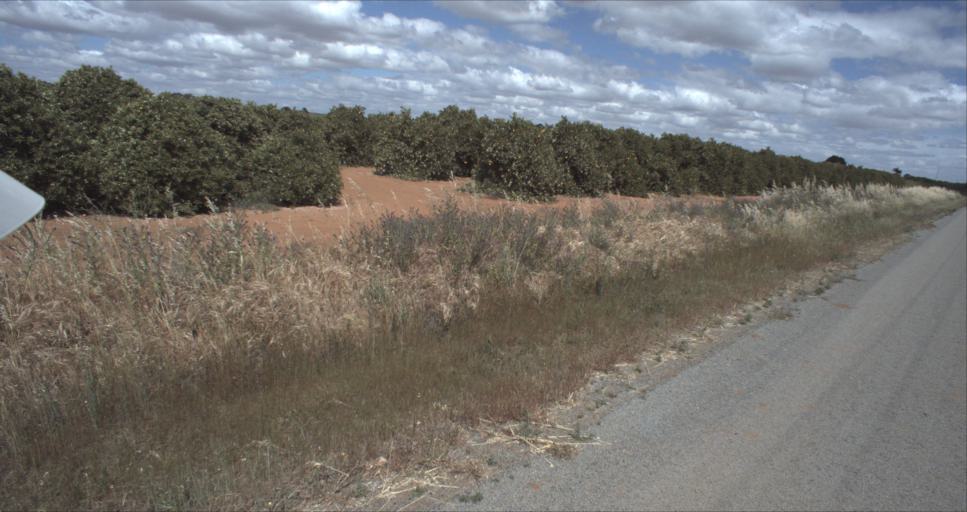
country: AU
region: New South Wales
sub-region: Leeton
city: Leeton
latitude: -34.5811
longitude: 146.3922
